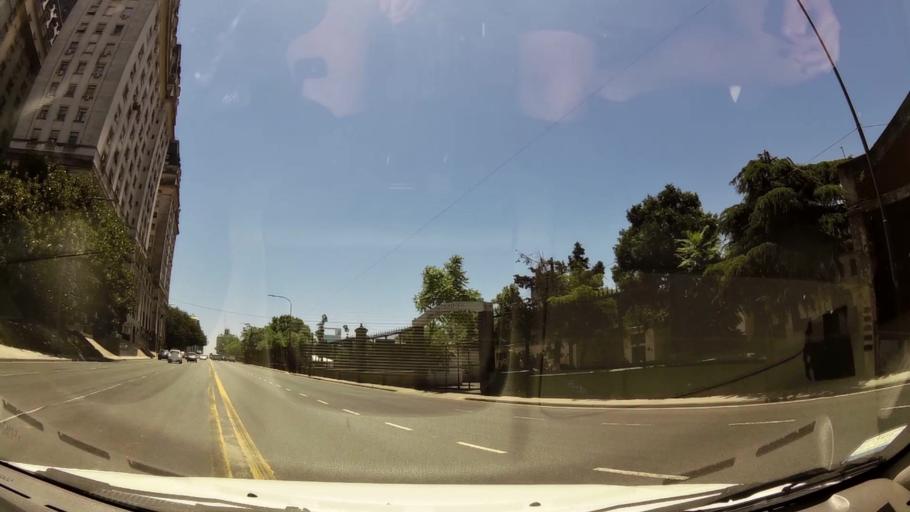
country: AR
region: Buenos Aires F.D.
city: Buenos Aires
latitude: -34.6110
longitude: -58.3673
